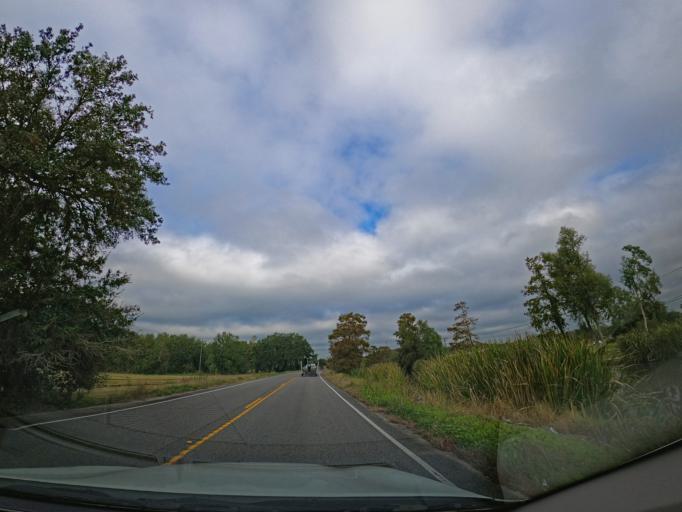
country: US
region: Louisiana
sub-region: Terrebonne Parish
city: Gray
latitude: 29.6232
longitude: -90.9086
